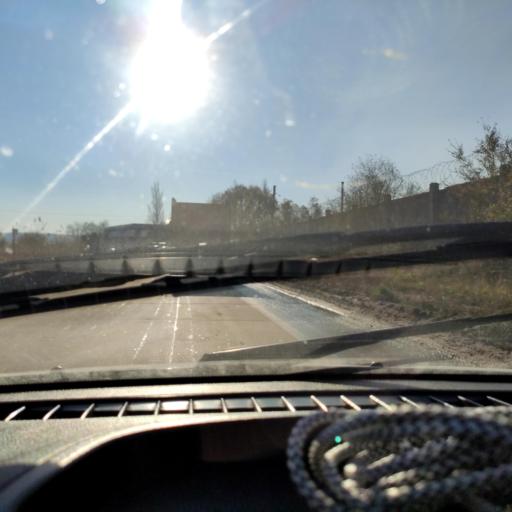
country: RU
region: Samara
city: Zhigulevsk
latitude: 53.4760
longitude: 49.4980
